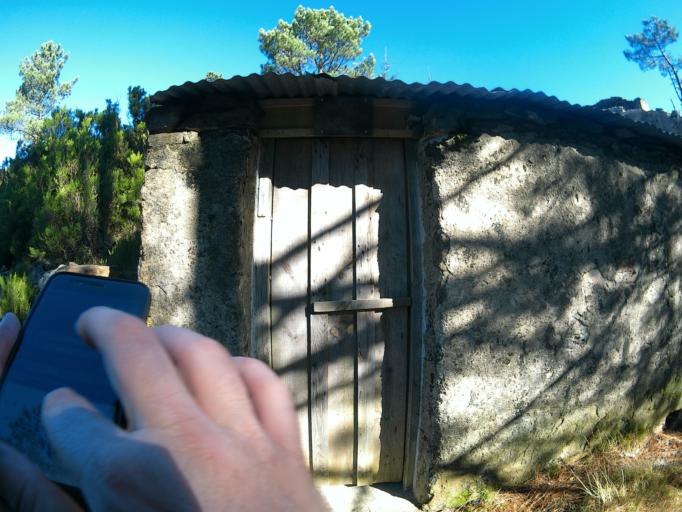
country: PT
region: Vila Real
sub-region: Mesao Frio
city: Mesao Frio
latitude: 41.2309
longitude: -7.9116
